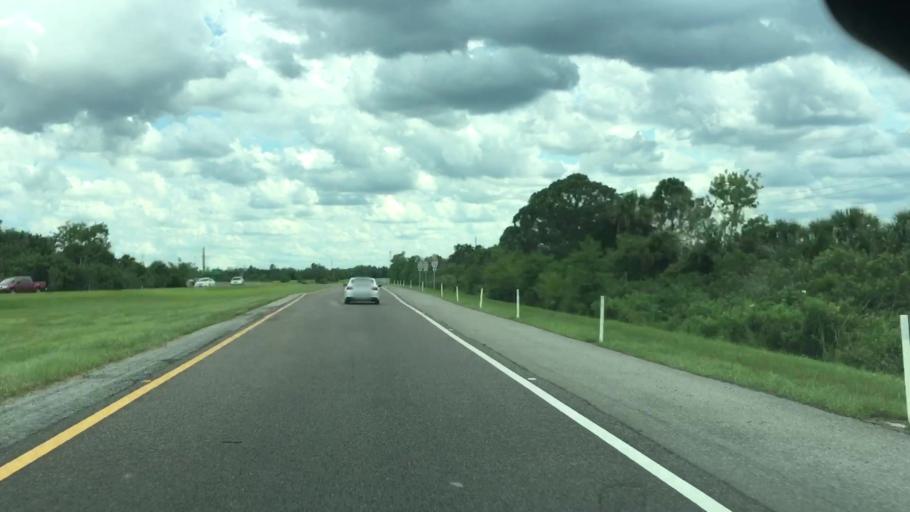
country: US
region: Florida
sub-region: Brevard County
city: Port Saint John
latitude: 28.5017
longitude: -80.8419
